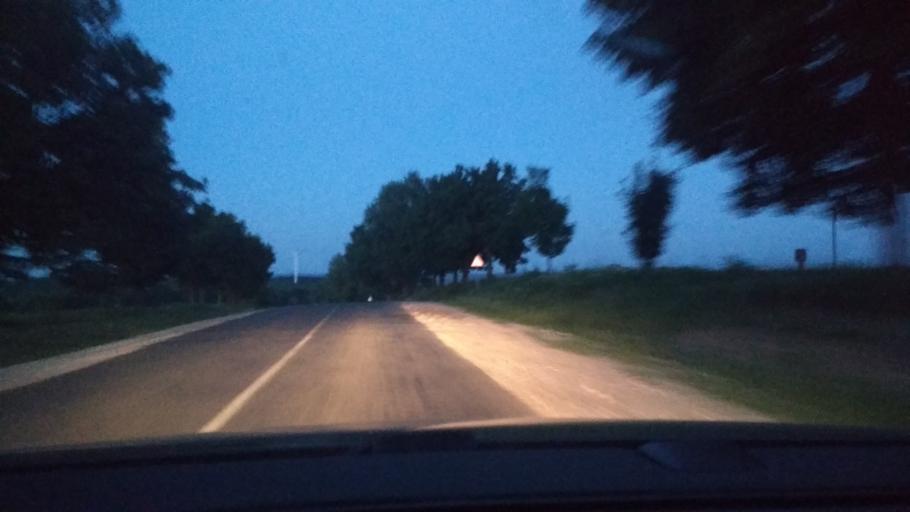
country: MD
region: Nisporeni
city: Nisporeni
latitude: 47.1570
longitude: 28.1849
